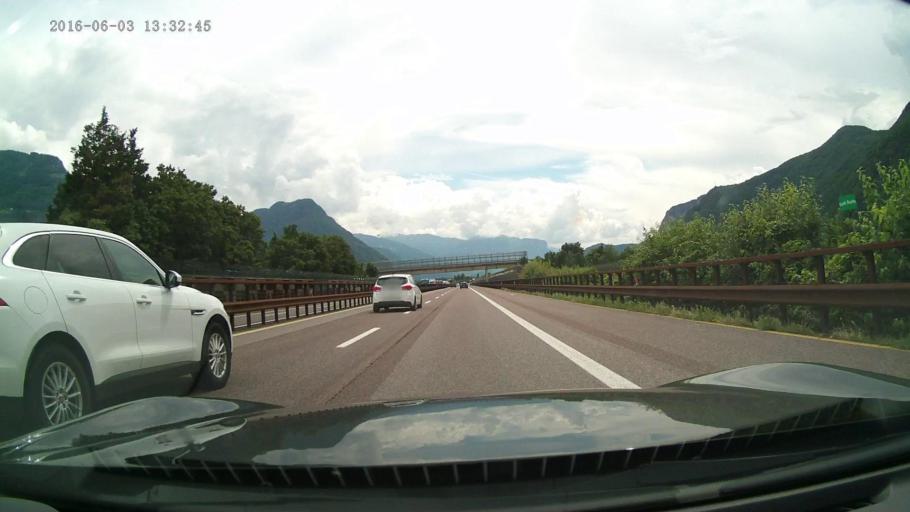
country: IT
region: Trentino-Alto Adige
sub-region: Bolzano
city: Vadena
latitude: 46.4303
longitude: 11.3169
